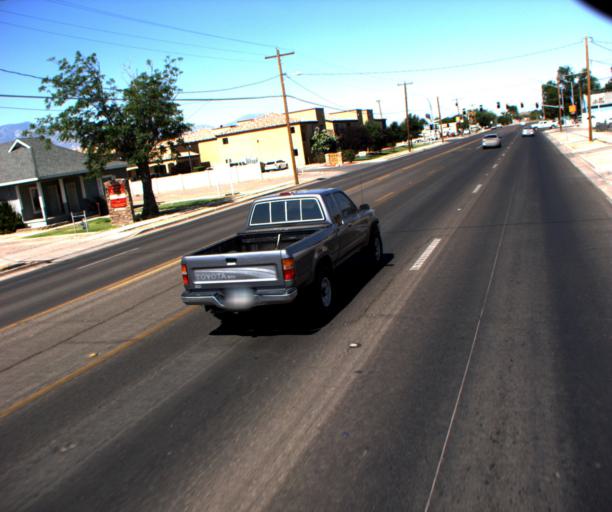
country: US
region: Arizona
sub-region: Graham County
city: Thatcher
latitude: 32.8492
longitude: -109.7655
